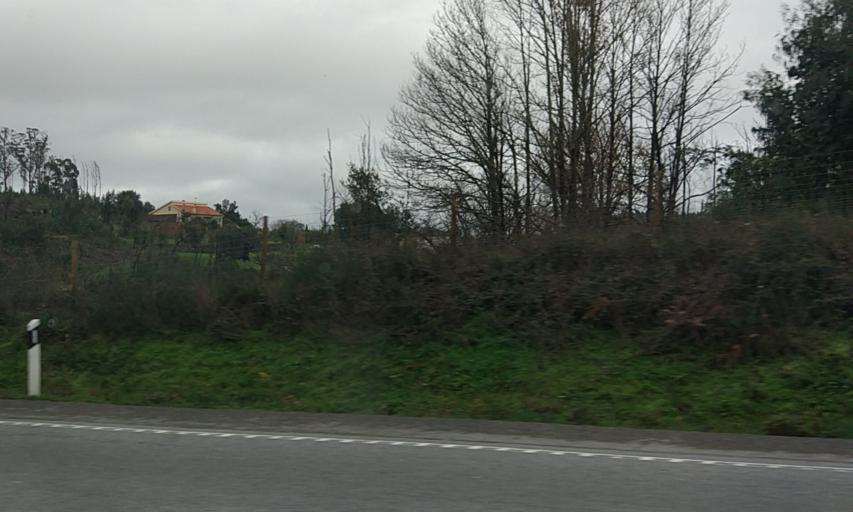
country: PT
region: Viseu
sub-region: Santa Comba Dao
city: Santa Comba Dao
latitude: 40.4212
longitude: -8.1199
